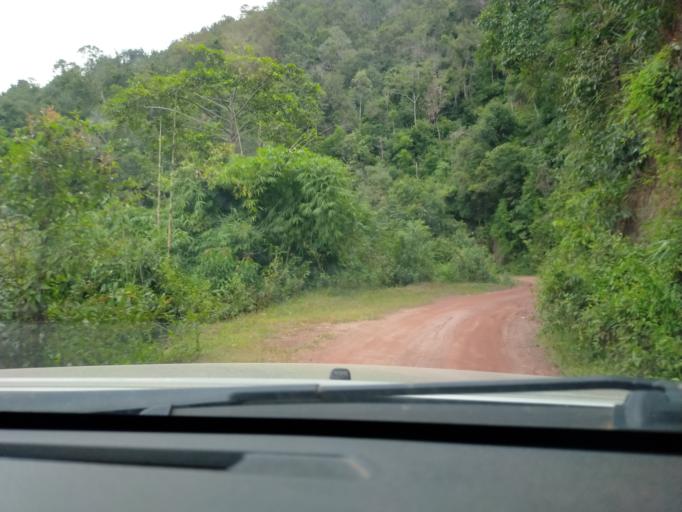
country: TH
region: Nan
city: Chaloem Phra Kiat
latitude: 19.7658
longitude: 101.3484
